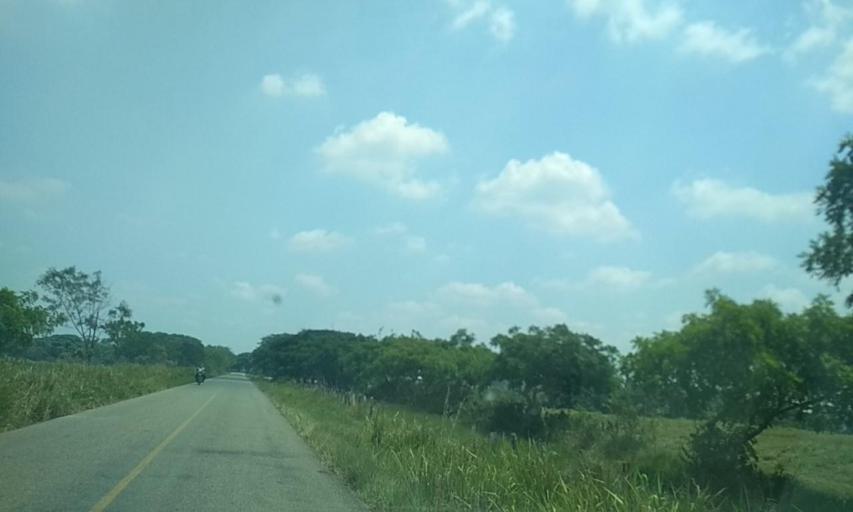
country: MX
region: Tabasco
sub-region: Cardenas
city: Poblado C-33 20 de Noviembre
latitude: 17.8494
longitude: -93.5712
